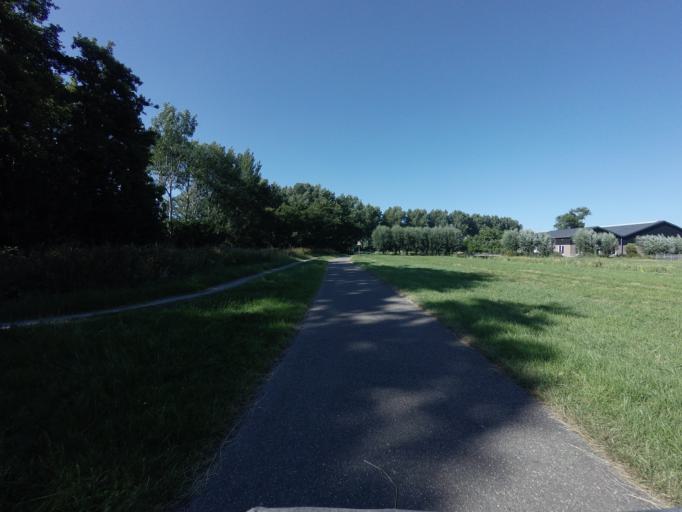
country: NL
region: South Holland
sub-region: Bodegraven-Reeuwijk
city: Bodegraven
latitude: 52.0650
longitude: 4.7532
